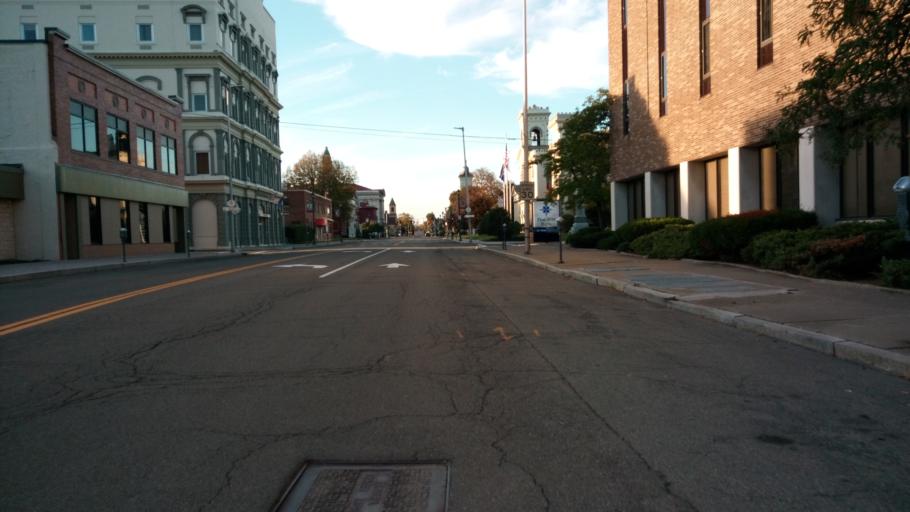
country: US
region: New York
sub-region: Chemung County
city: Elmira
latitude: 42.0895
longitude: -76.8015
